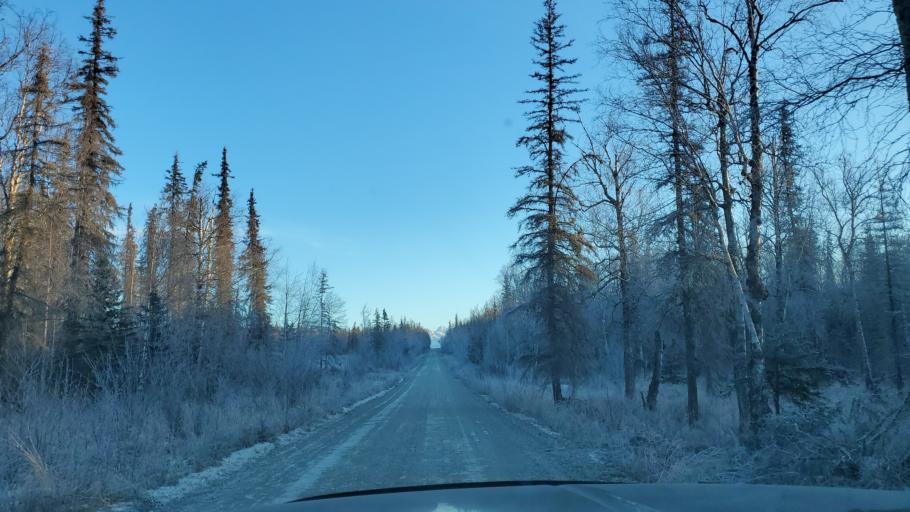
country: US
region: Alaska
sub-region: Matanuska-Susitna Borough
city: Lakes
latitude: 61.6428
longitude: -149.3547
